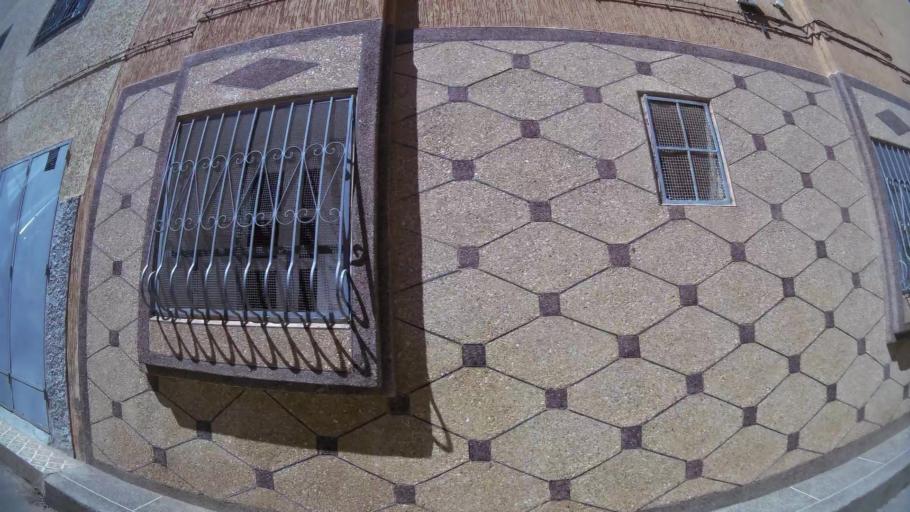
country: MA
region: Oriental
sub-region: Oujda-Angad
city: Oujda
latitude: 34.6706
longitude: -1.9306
